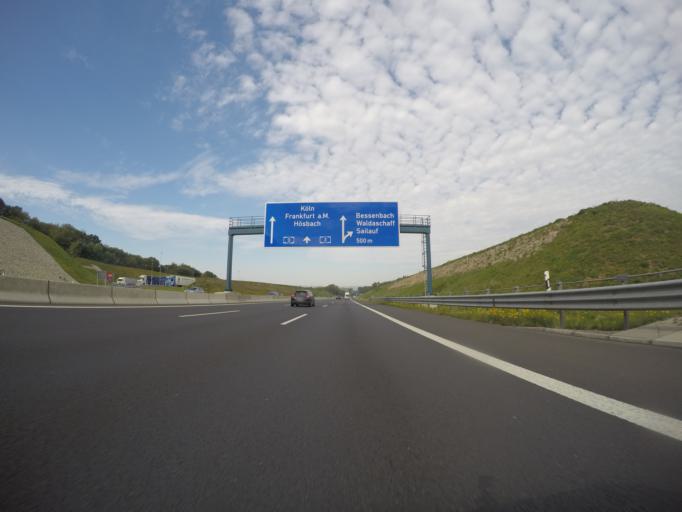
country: DE
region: Bavaria
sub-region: Regierungsbezirk Unterfranken
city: Waldaschaff
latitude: 49.9820
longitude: 9.2650
